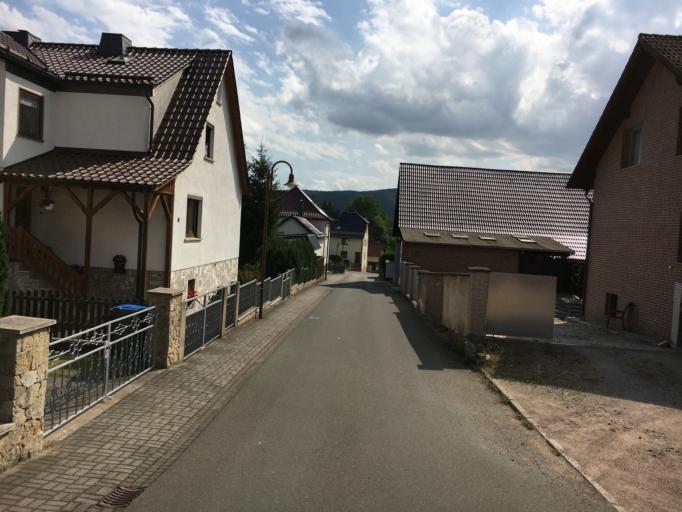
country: DE
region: Thuringia
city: Breitungen
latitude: 50.7623
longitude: 10.3324
